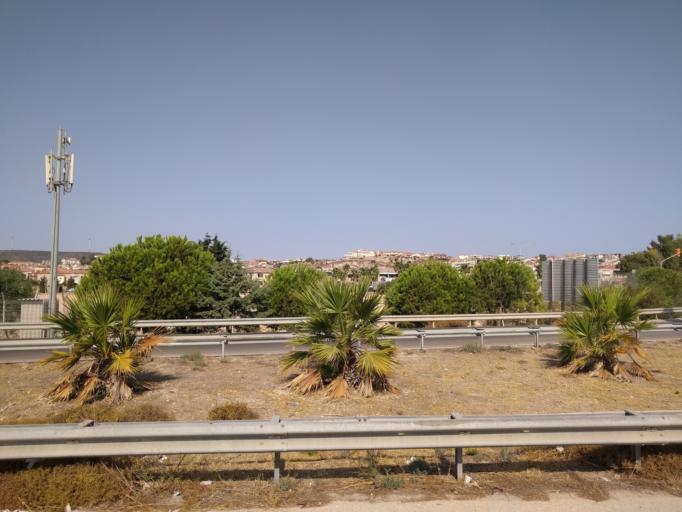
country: TR
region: Izmir
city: Alacati
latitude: 38.2877
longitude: 26.3847
